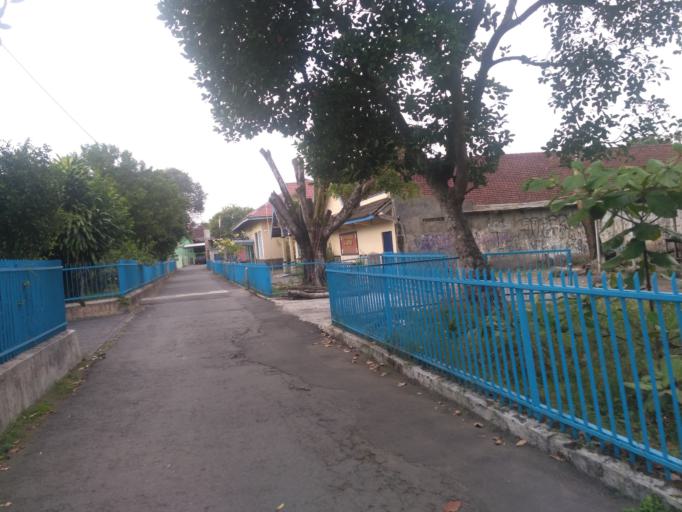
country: ID
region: Daerah Istimewa Yogyakarta
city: Melati
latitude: -7.7523
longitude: 110.3677
